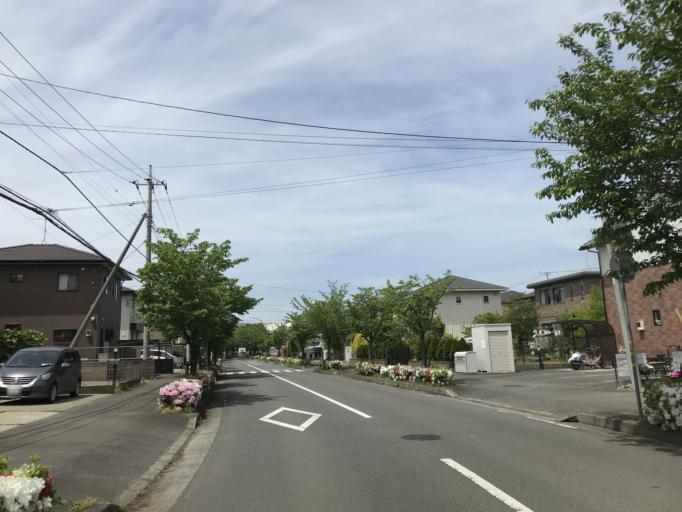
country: JP
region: Ibaraki
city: Mitsukaido
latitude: 35.9815
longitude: 139.9621
